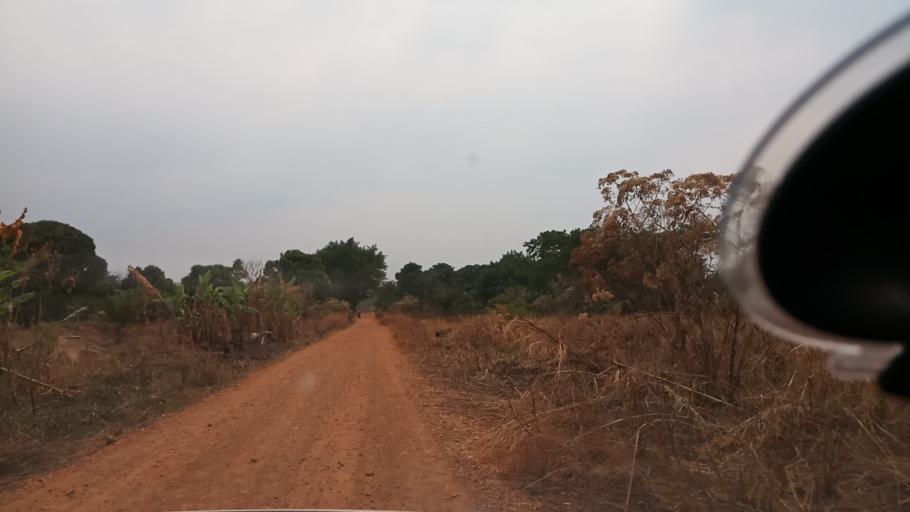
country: ZM
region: Luapula
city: Nchelenge
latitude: -9.0872
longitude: 28.3331
